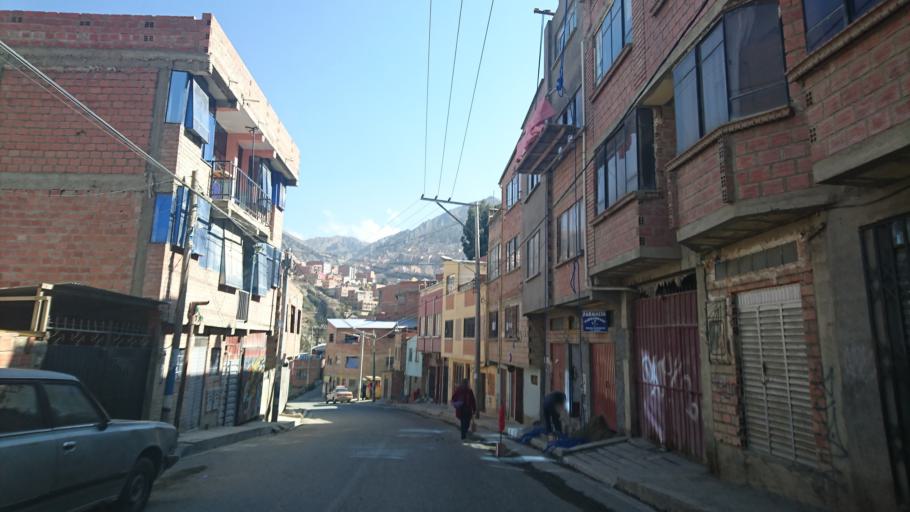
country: BO
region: La Paz
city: La Paz
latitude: -16.4765
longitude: -68.1136
